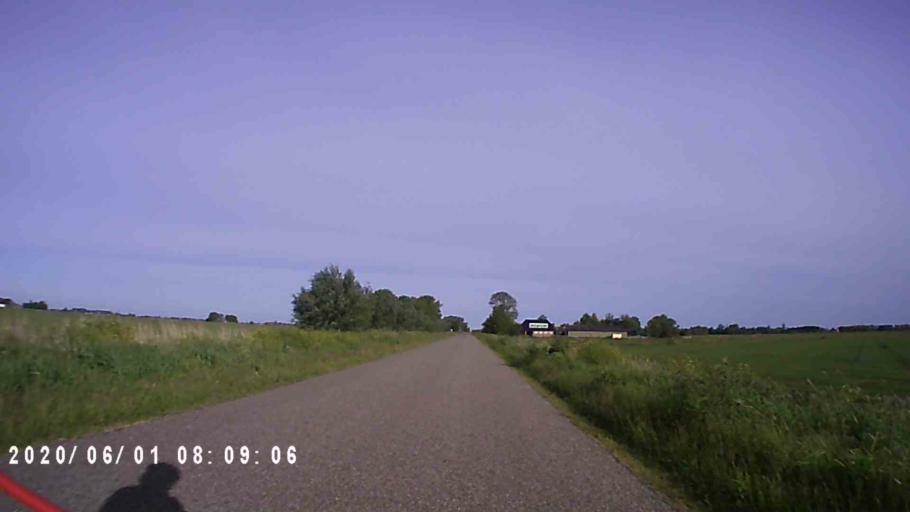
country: NL
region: Friesland
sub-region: Gemeente Ferwerderadiel
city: Burdaard
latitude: 53.2846
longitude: 5.8955
